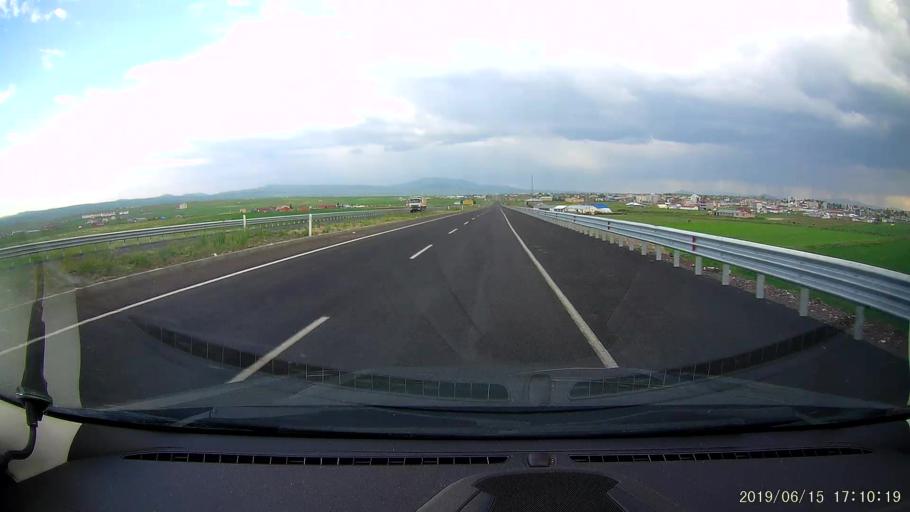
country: TR
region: Kars
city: Kars
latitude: 40.6235
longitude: 43.1338
